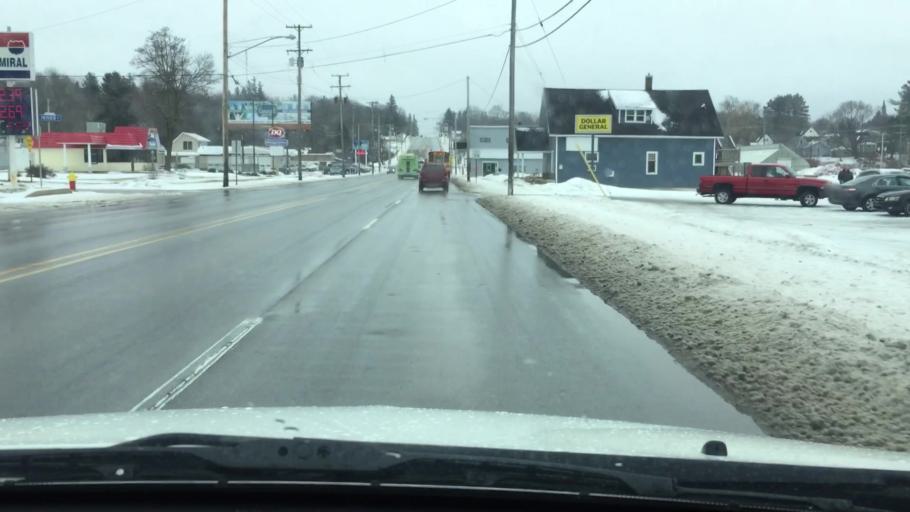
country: US
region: Michigan
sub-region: Wexford County
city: Cadillac
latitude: 44.2439
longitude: -85.3965
